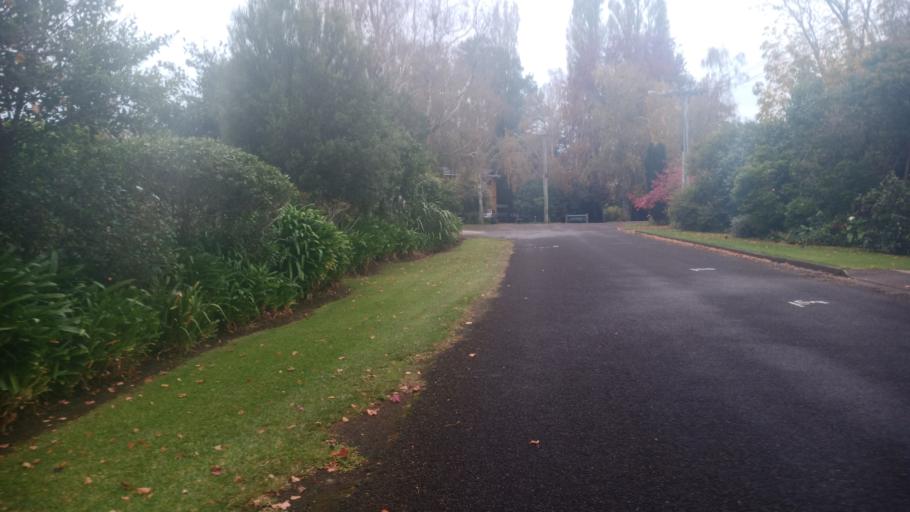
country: NZ
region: Gisborne
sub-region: Gisborne District
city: Gisborne
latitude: -38.6653
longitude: 178.0399
